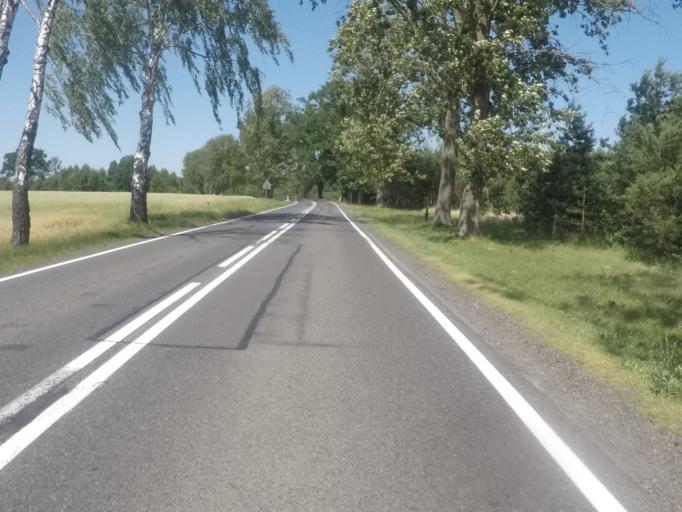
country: PL
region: Podlasie
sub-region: Powiat siemiatycki
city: Siemiatycze
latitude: 52.4779
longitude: 22.8782
